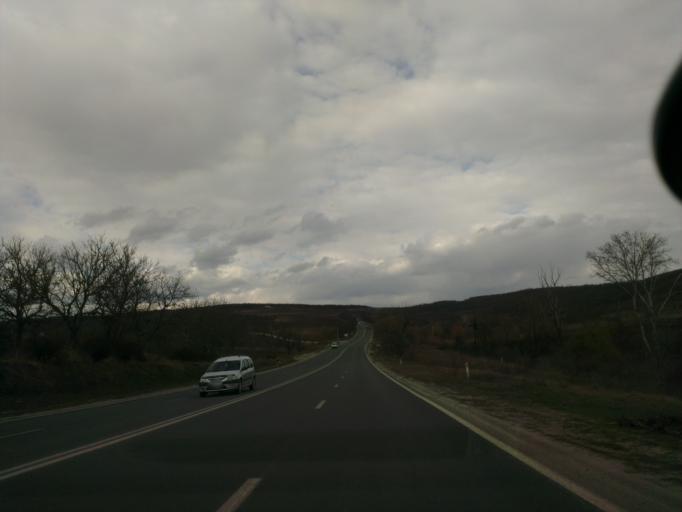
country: MD
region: Laloveni
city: Ialoveni
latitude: 46.9261
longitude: 28.6971
